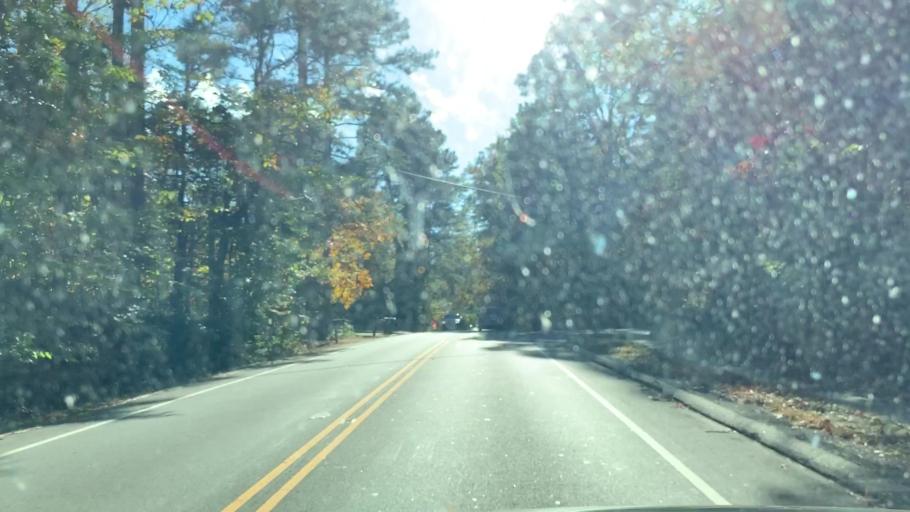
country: US
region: Virginia
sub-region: James City County
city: Williamsburg
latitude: 37.2493
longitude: -76.7363
